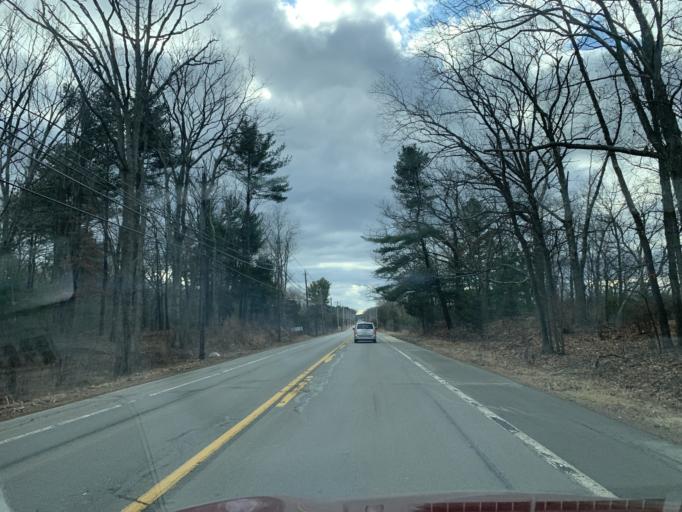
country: US
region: Massachusetts
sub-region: Essex County
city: Newburyport
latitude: 42.7743
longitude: -70.8853
